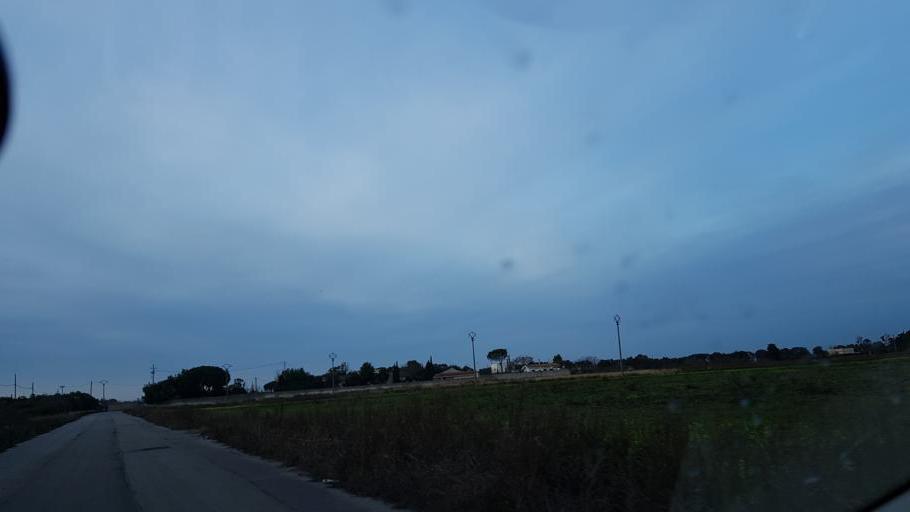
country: IT
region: Apulia
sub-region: Provincia di Brindisi
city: Brindisi
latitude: 40.6534
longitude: 17.9139
